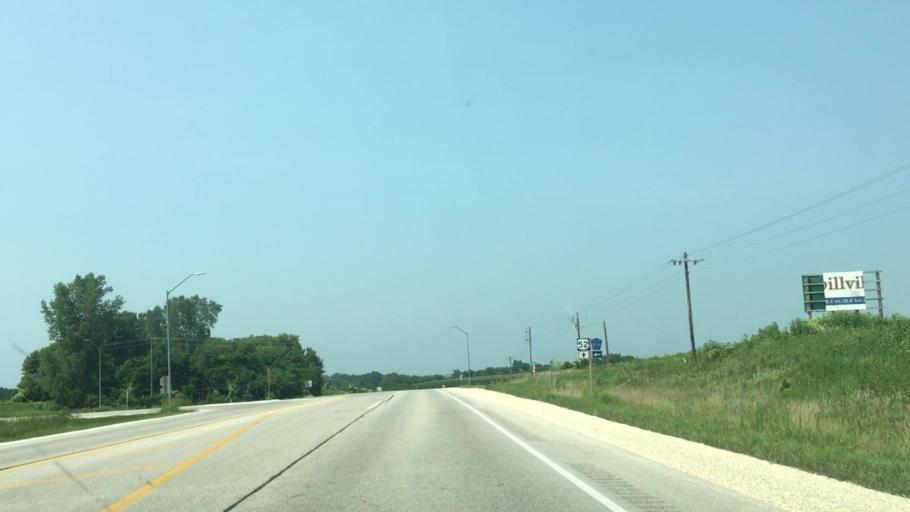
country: US
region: Iowa
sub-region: Winneshiek County
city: Decorah
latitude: 43.2046
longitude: -91.8778
